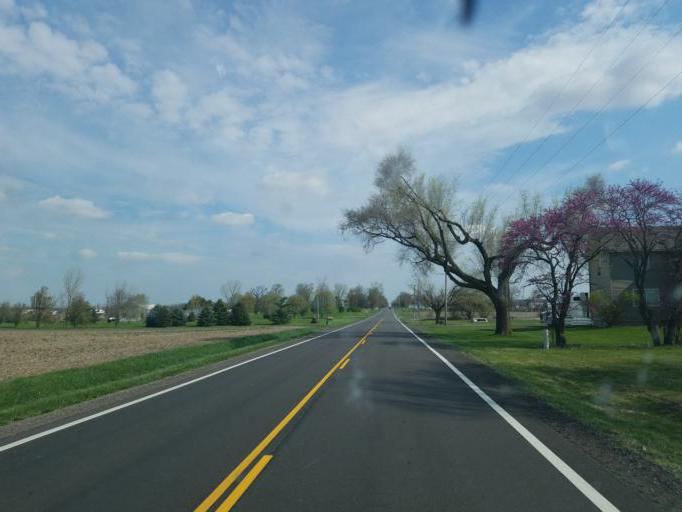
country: US
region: Ohio
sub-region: Crawford County
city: Bucyrus
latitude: 40.6823
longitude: -83.0105
